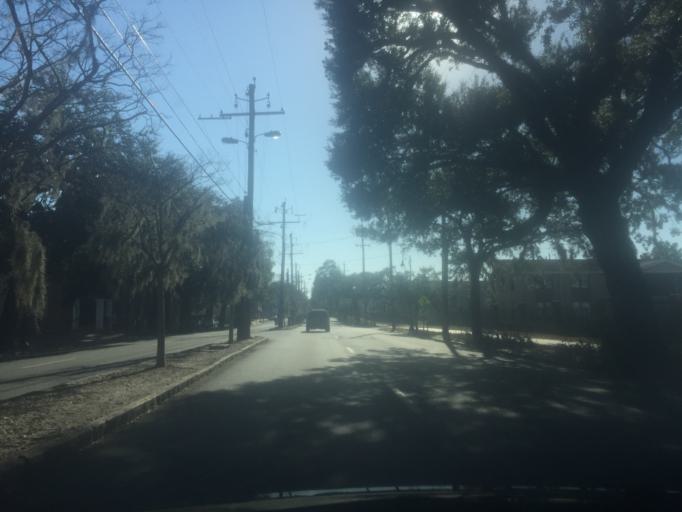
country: US
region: Georgia
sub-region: Chatham County
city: Savannah
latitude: 32.0667
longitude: -81.1024
